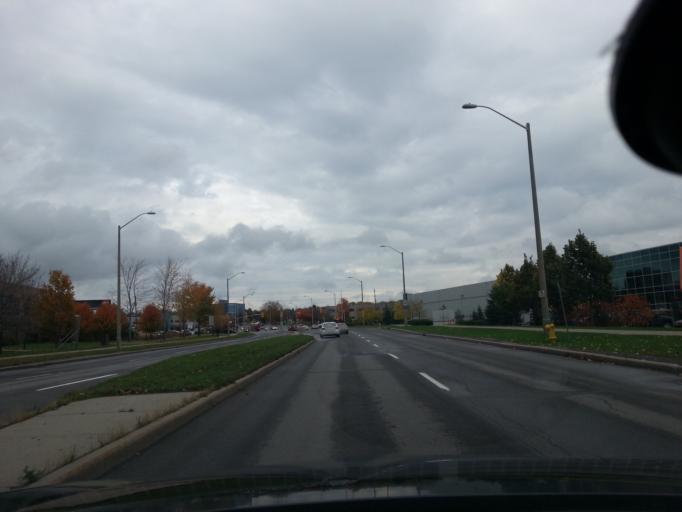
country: CA
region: Ontario
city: Bells Corners
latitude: 45.2985
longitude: -75.9126
